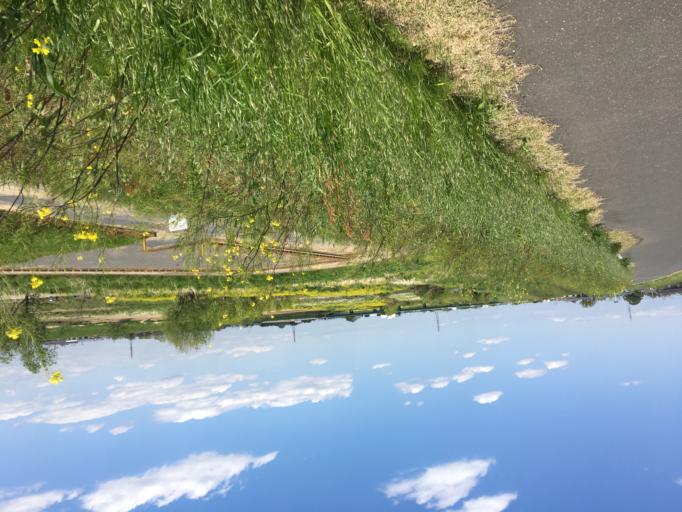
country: JP
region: Saitama
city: Kawagoe
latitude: 35.9365
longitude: 139.4628
